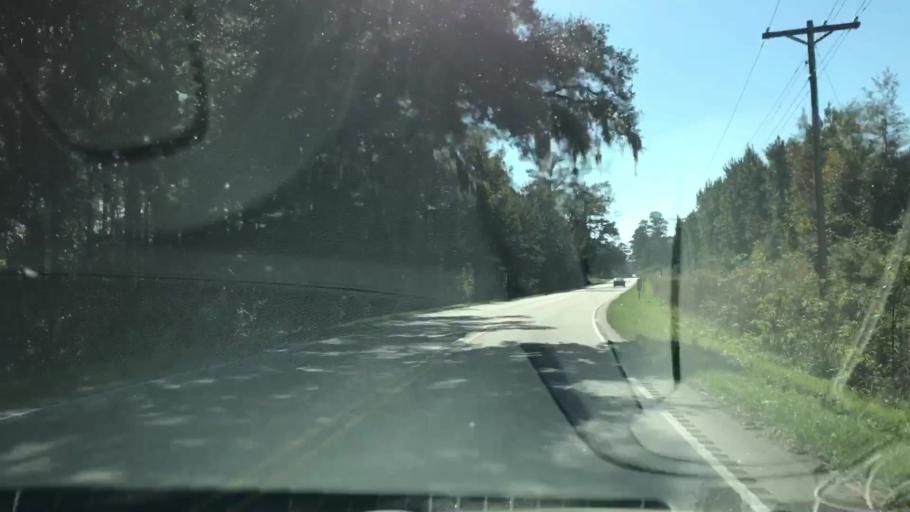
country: US
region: South Carolina
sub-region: Jasper County
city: Ridgeland
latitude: 32.5208
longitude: -80.8909
